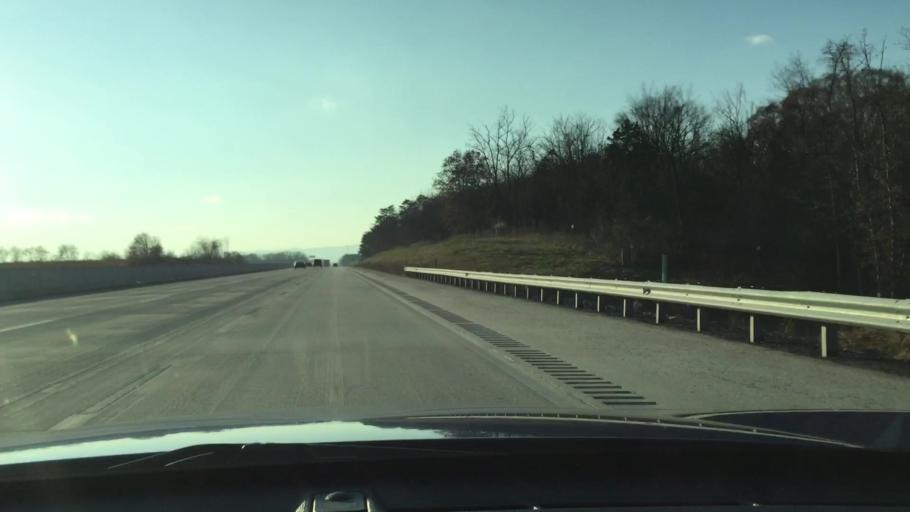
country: US
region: Pennsylvania
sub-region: Cumberland County
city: Newville
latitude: 40.1904
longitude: -77.4489
